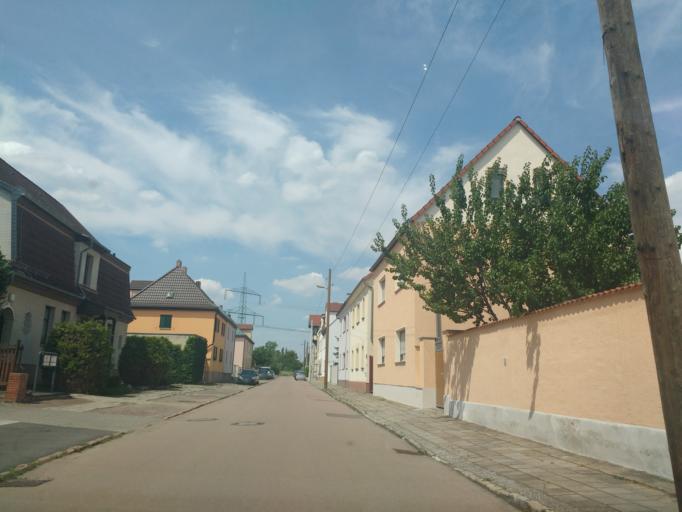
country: DE
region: Saxony-Anhalt
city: Dieskau
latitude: 51.4579
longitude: 12.0349
